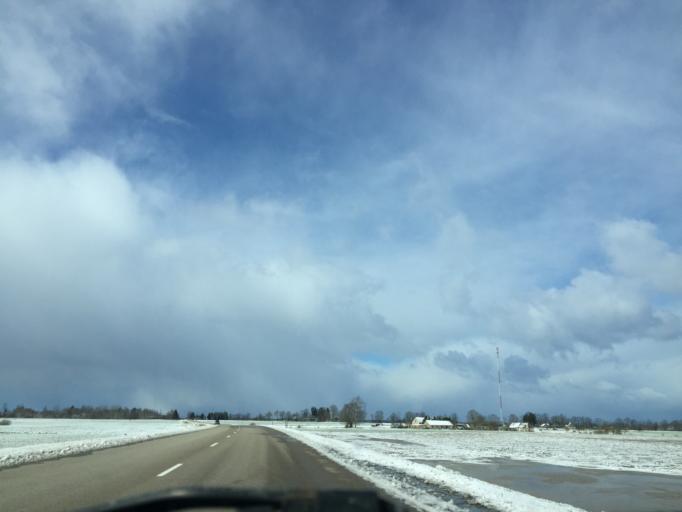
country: LV
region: Talsu Rajons
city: Stende
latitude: 57.2103
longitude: 22.5141
